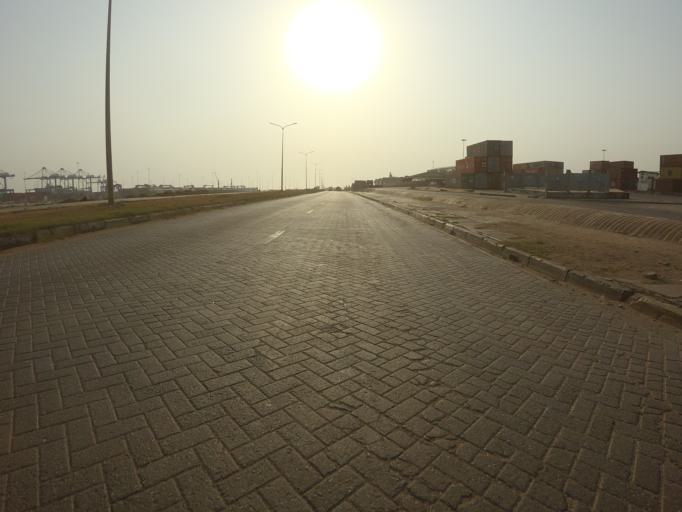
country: GH
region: Greater Accra
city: Tema
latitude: 5.6233
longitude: -0.0093
